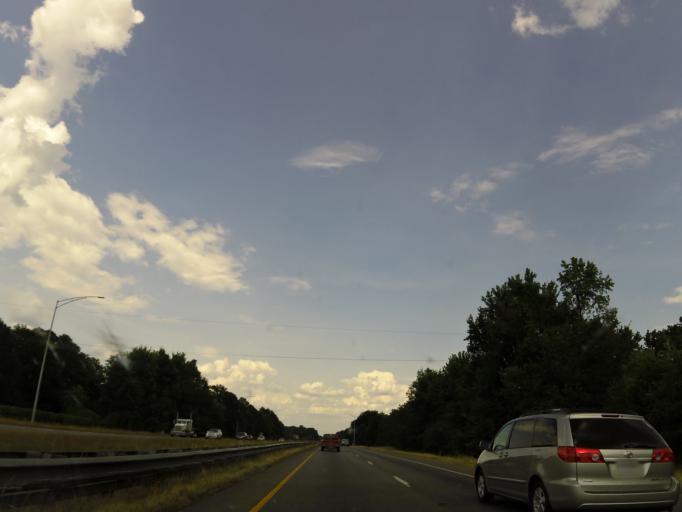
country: US
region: Alabama
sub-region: Tuscaloosa County
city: Holt
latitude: 33.1758
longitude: -87.4961
